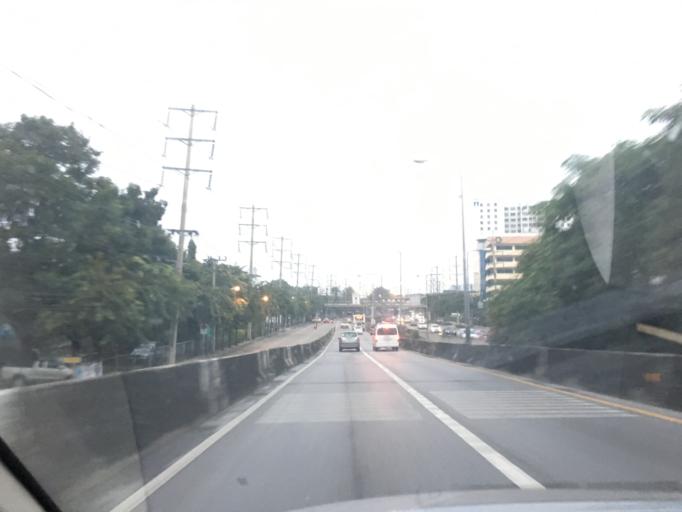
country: TH
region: Bangkok
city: Bang Kho Laem
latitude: 13.6897
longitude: 100.5077
